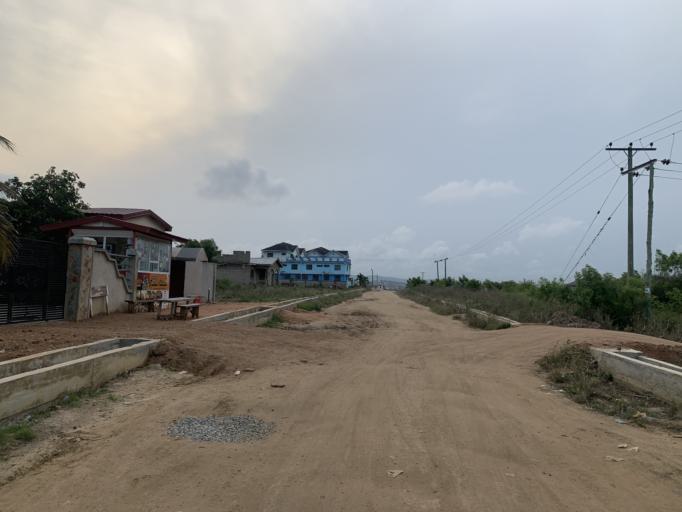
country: GH
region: Central
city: Winneba
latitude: 5.3822
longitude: -0.6253
